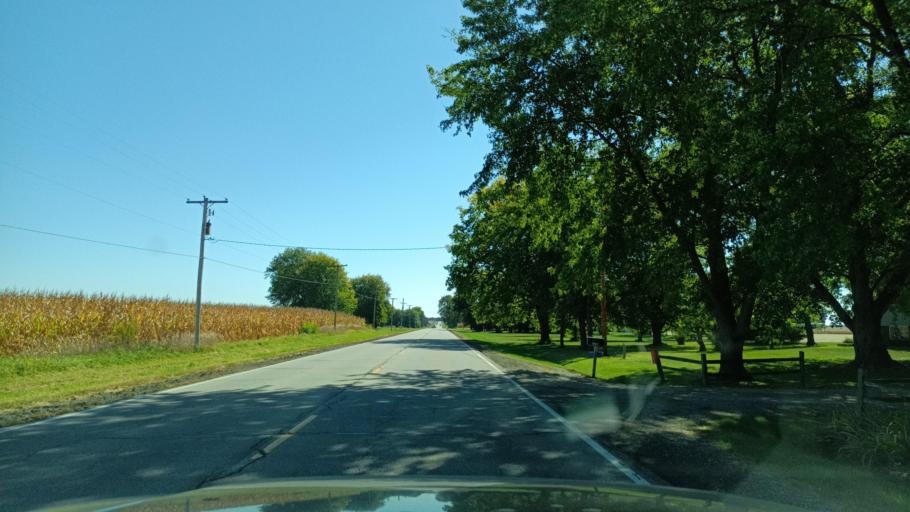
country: US
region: Illinois
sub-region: Peoria County
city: Elmwood
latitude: 40.8288
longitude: -89.8645
